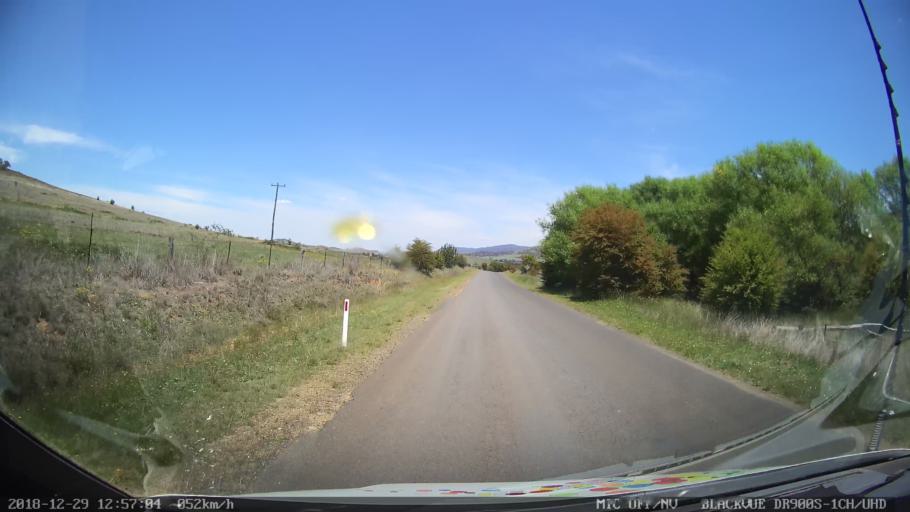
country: AU
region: Australian Capital Territory
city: Macarthur
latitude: -35.7054
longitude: 149.1797
